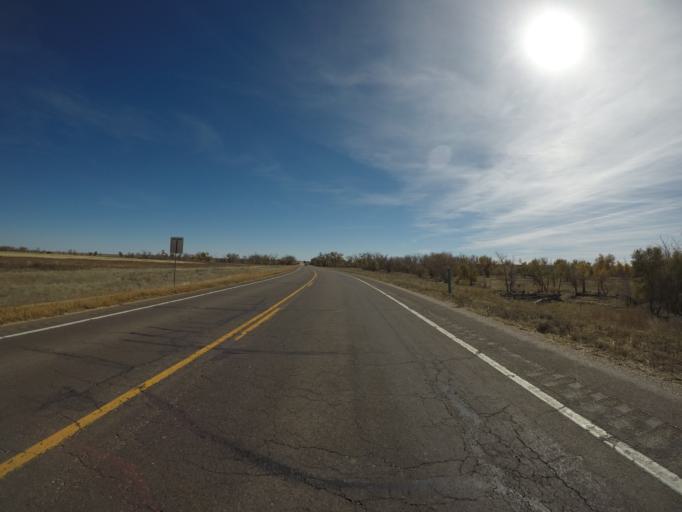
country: US
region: Colorado
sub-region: Yuma County
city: Yuma
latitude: 39.6601
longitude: -102.8500
